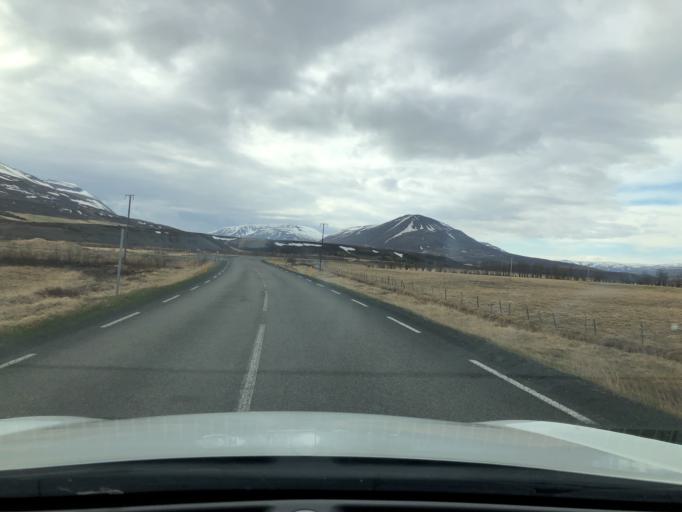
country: IS
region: Northeast
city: Akureyri
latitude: 65.7748
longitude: -17.9167
